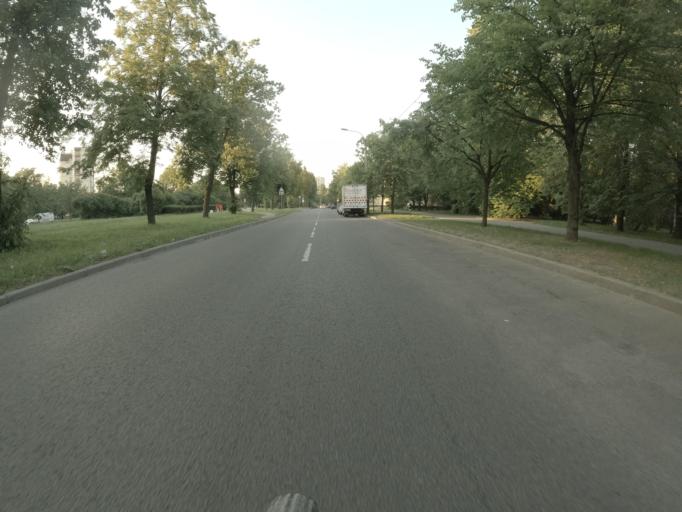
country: RU
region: St.-Petersburg
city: Dachnoye
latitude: 59.8447
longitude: 30.2674
